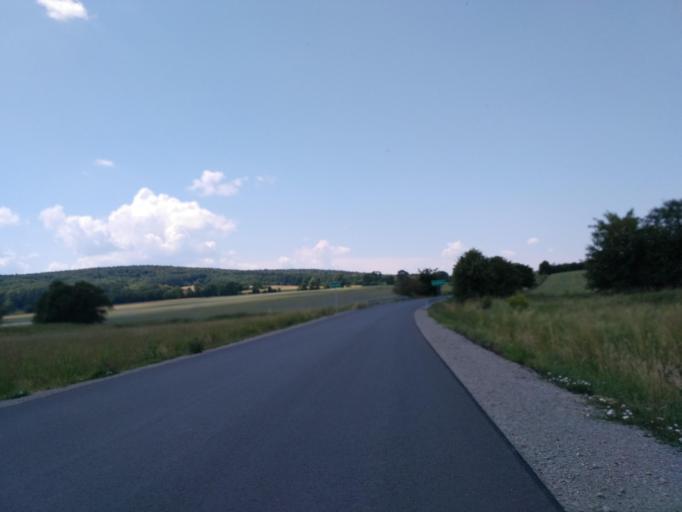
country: PL
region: Subcarpathian Voivodeship
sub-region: Powiat sanocki
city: Strachocina
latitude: 49.5743
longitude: 22.1312
